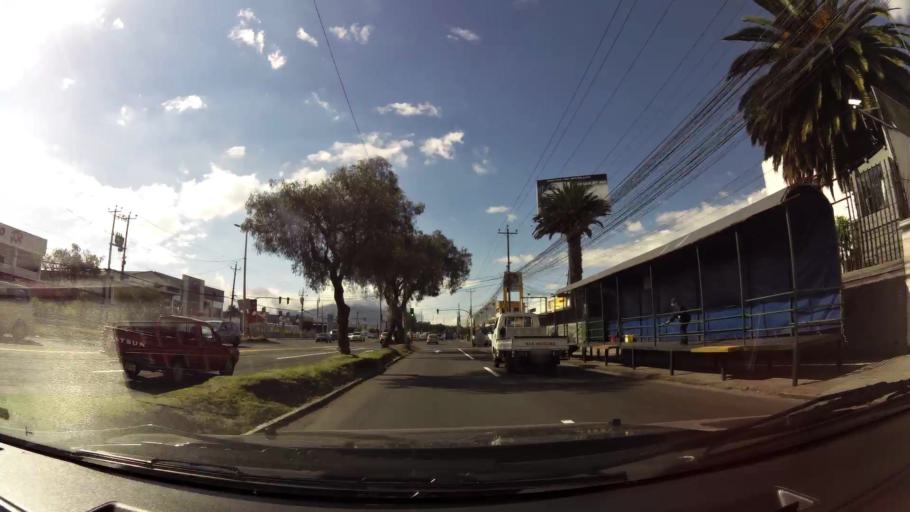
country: EC
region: Pichincha
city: Quito
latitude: -0.1122
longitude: -78.4789
